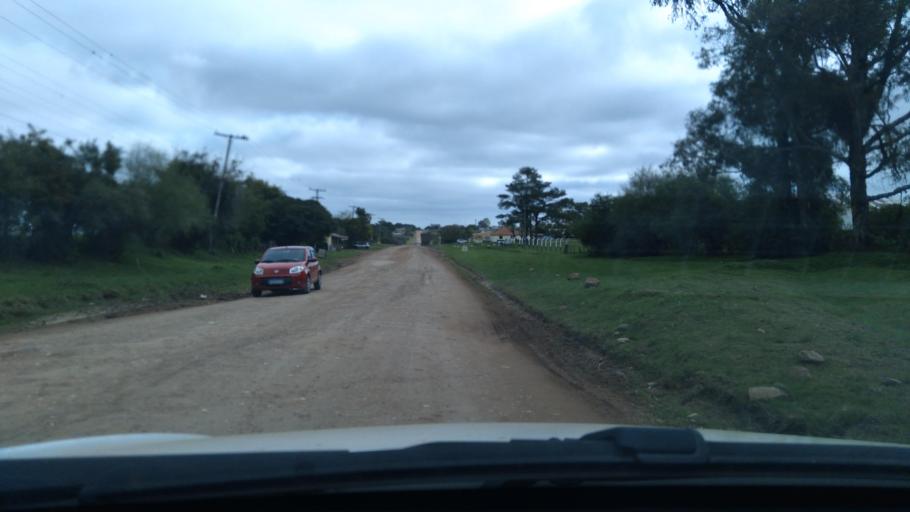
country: BR
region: Rio Grande do Sul
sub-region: Dom Pedrito
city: Dom Pedrito
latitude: -30.9822
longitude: -54.6474
